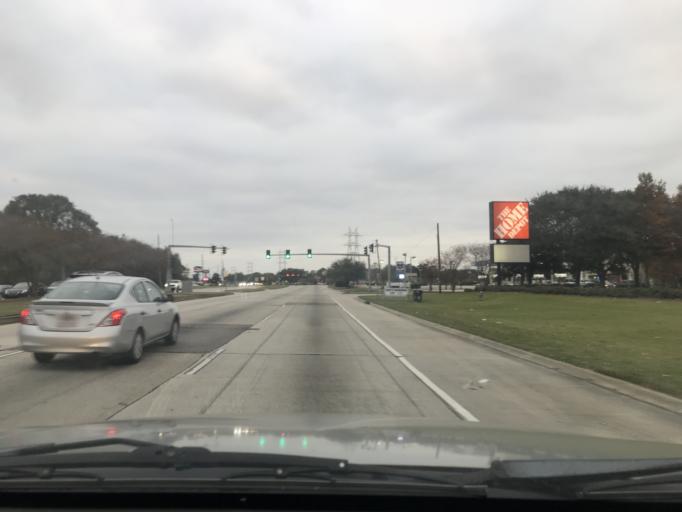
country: US
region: Louisiana
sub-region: Jefferson Parish
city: Woodmere
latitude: 29.8747
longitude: -90.0904
